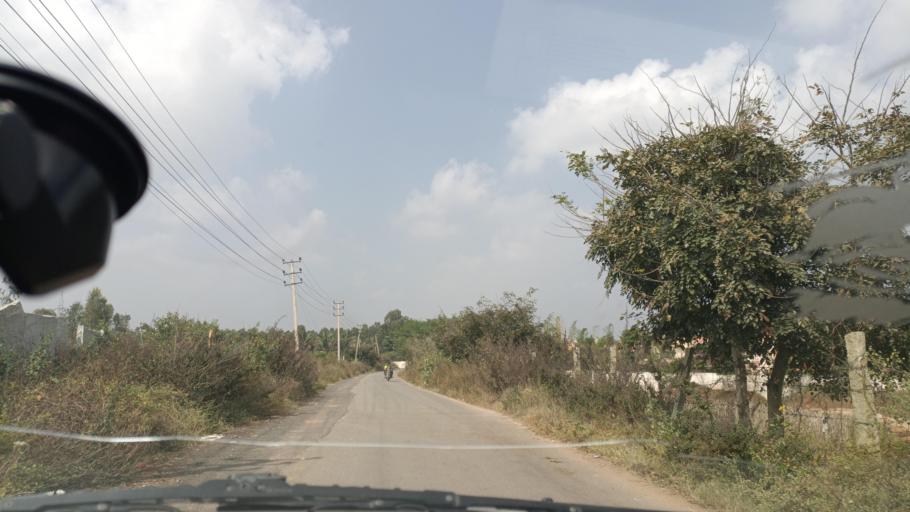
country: IN
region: Karnataka
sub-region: Bangalore Urban
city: Yelahanka
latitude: 13.1500
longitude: 77.6345
